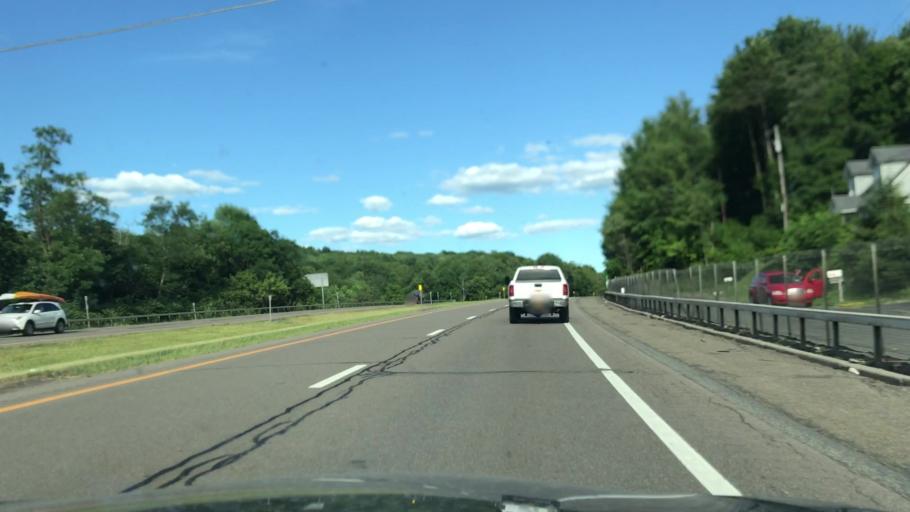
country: US
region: New York
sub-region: Broome County
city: Chenango Bridge
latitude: 42.1013
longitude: -75.8037
